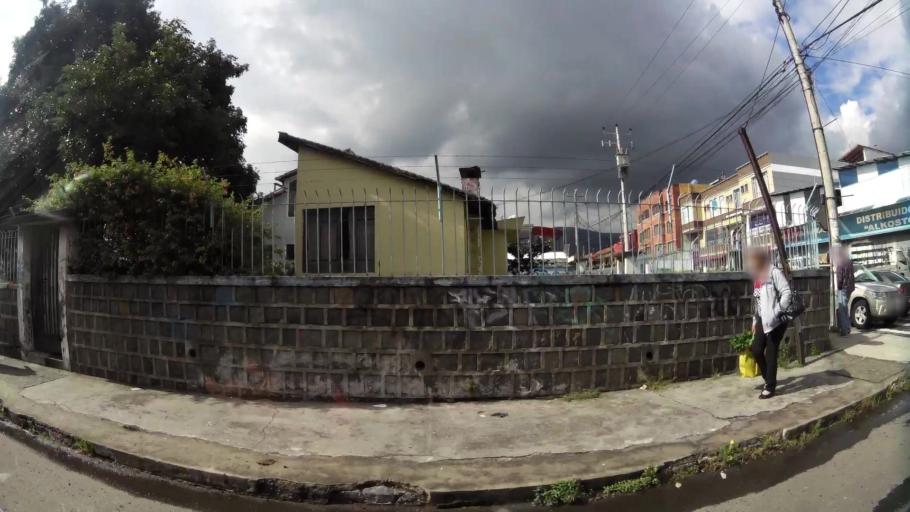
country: EC
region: Pichincha
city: Sangolqui
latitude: -0.3015
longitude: -78.4589
